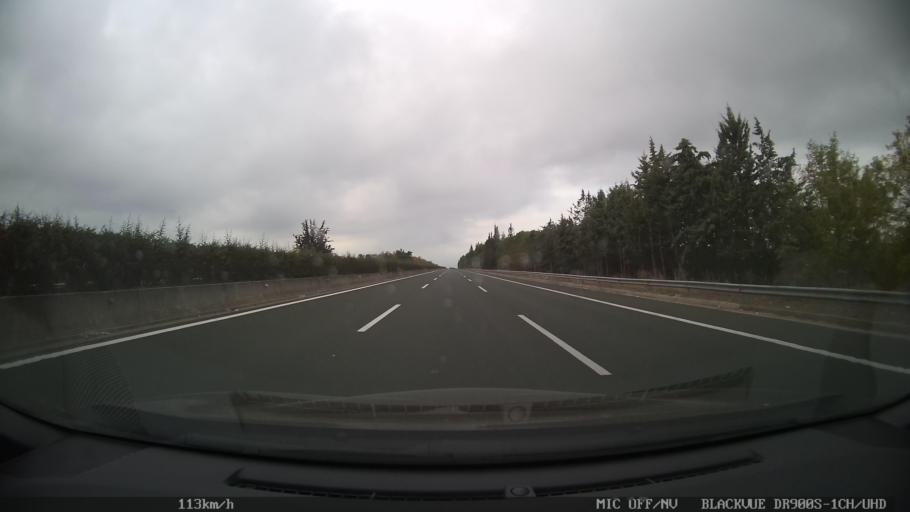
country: GR
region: Central Macedonia
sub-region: Nomos Pierias
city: Kitros
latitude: 40.3544
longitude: 22.5980
